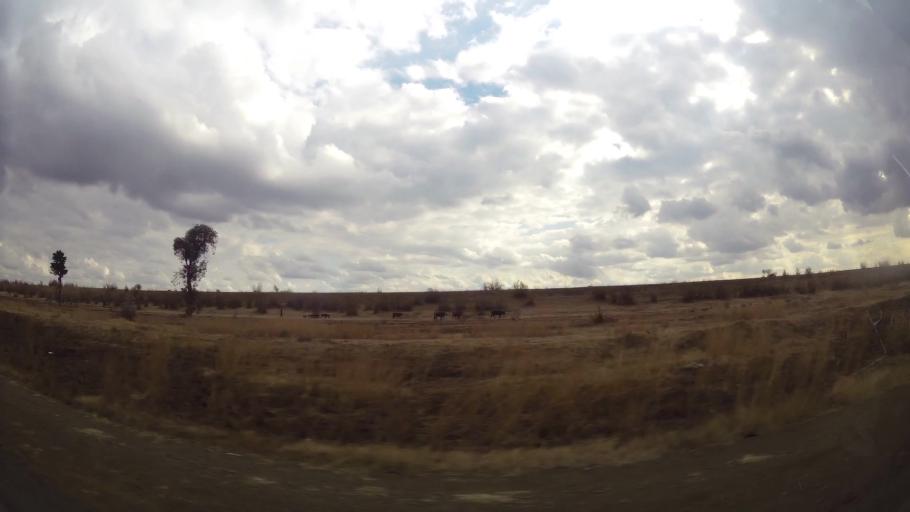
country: ZA
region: Orange Free State
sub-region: Fezile Dabi District Municipality
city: Sasolburg
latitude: -26.8739
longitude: 27.8871
